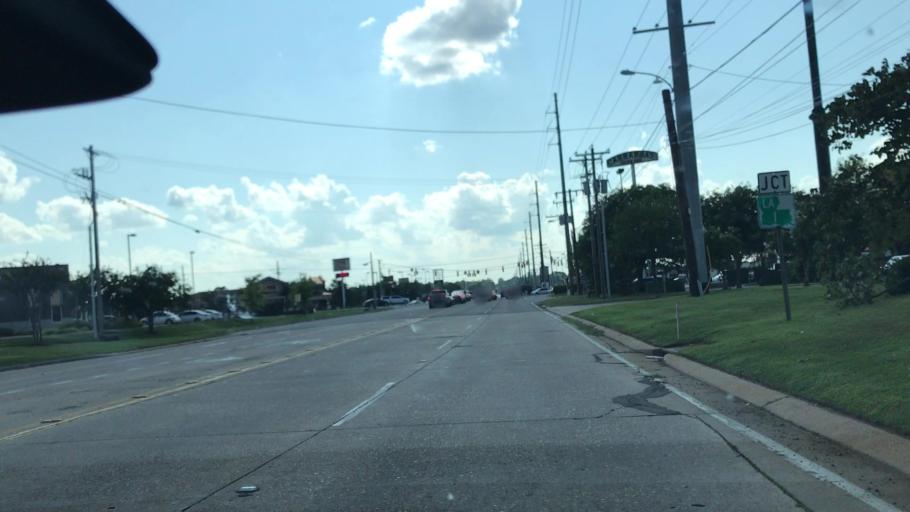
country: US
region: Louisiana
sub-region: Bossier Parish
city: Bossier City
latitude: 32.4435
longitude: -93.7167
